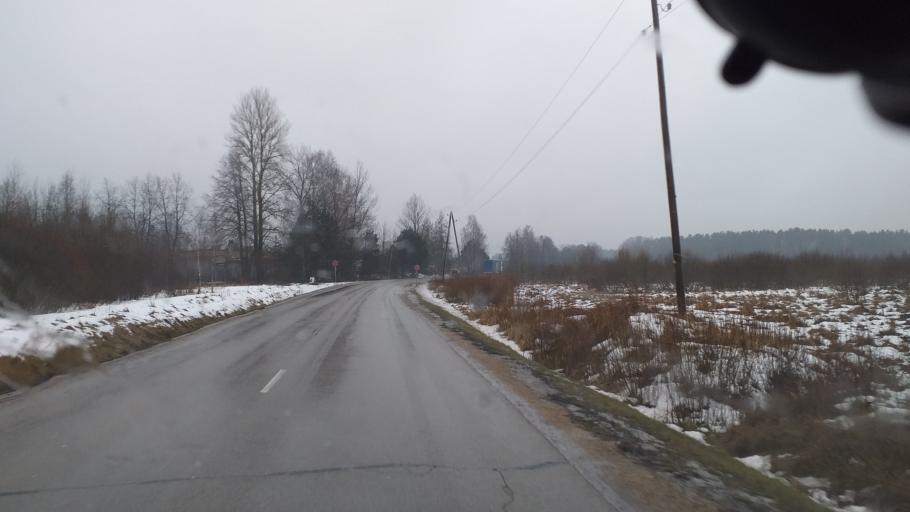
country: LV
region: Babite
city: Pinki
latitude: 56.9696
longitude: 23.9687
